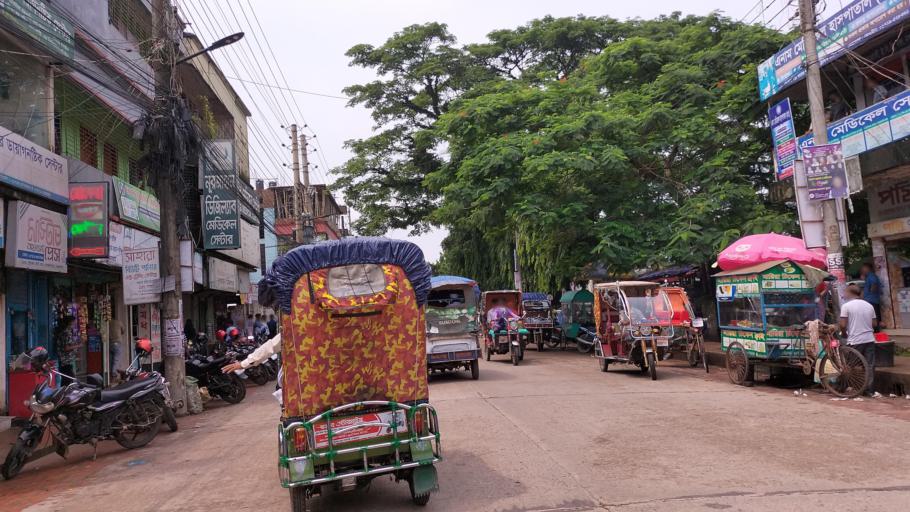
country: BD
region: Dhaka
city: Netrakona
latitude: 24.8784
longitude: 90.7309
